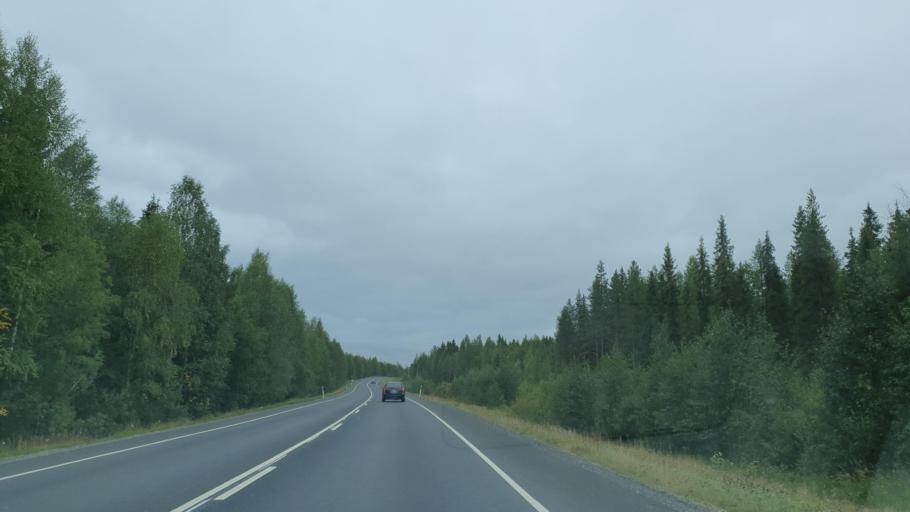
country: FI
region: Lapland
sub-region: Rovaniemi
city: Rovaniemi
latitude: 66.5946
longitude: 25.5995
